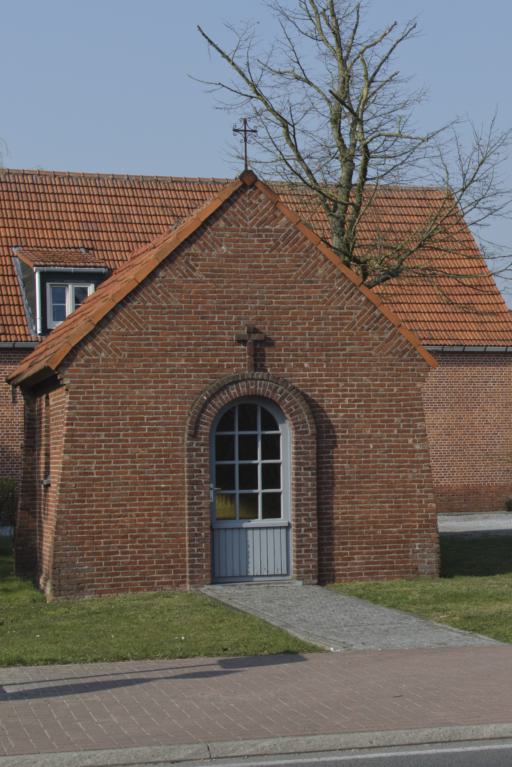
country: BE
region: Flanders
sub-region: Provincie Antwerpen
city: Retie
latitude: 51.2752
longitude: 5.1171
